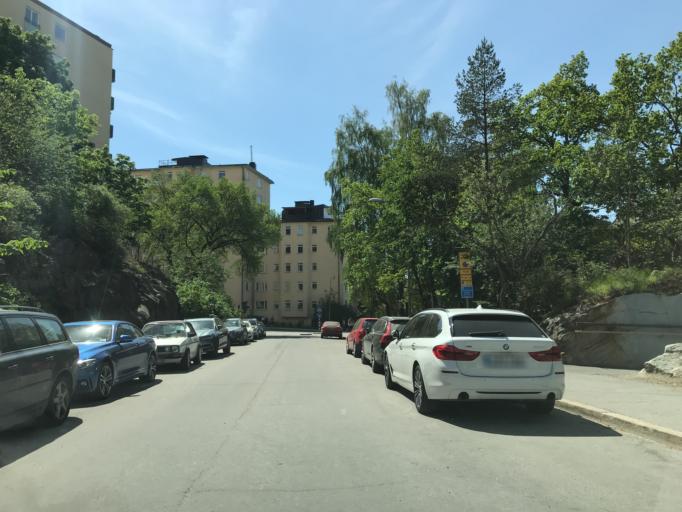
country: SE
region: Stockholm
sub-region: Stockholms Kommun
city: OEstermalm
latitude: 59.3484
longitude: 18.0949
